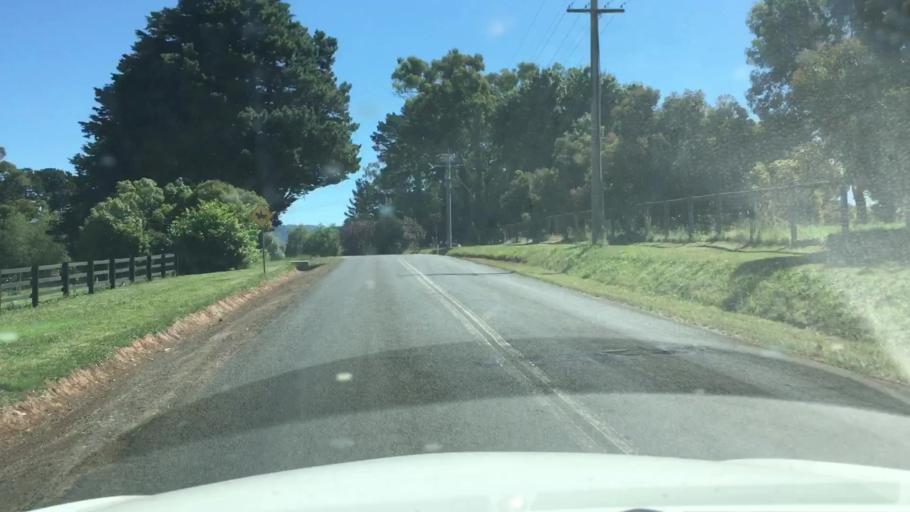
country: AU
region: Victoria
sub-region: Yarra Ranges
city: Mount Evelyn
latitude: -37.8127
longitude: 145.4242
